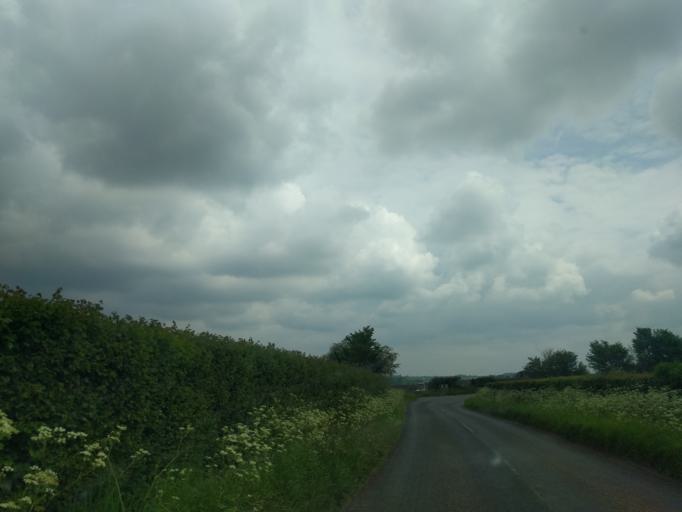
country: GB
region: England
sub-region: Somerset
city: Langport
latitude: 51.0565
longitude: -2.8137
